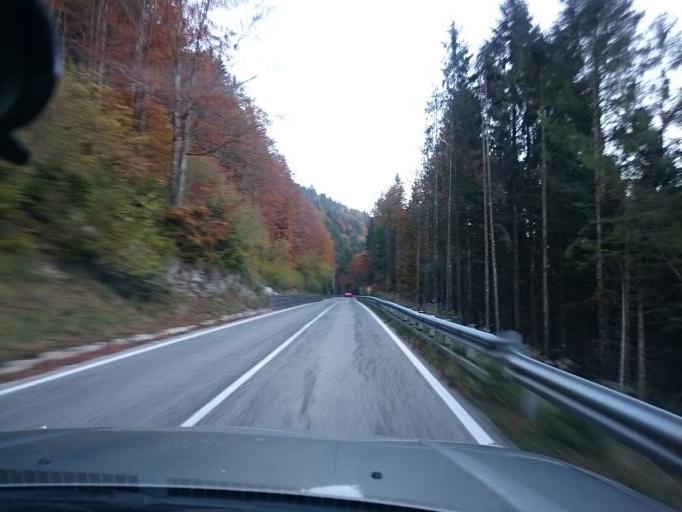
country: IT
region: Veneto
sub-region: Provincia di Vicenza
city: Roana
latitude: 45.9030
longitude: 11.4620
